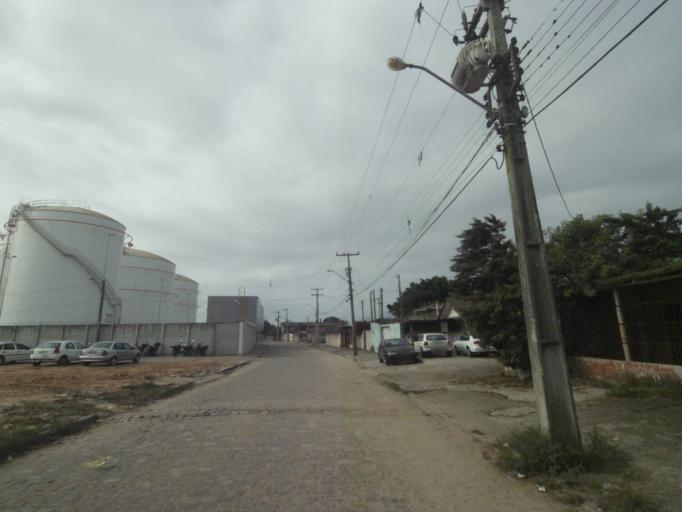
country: BR
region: Parana
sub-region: Paranagua
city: Paranagua
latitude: -25.5131
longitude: -48.5313
